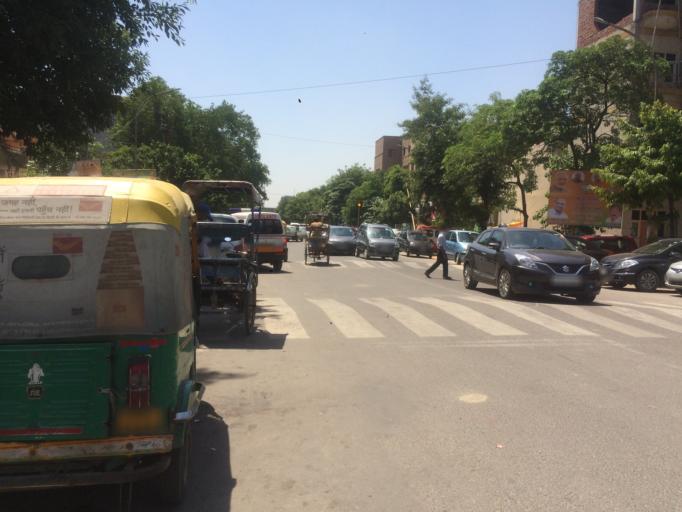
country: IN
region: Uttar Pradesh
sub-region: Gautam Buddha Nagar
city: Noida
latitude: 28.5776
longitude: 77.3320
